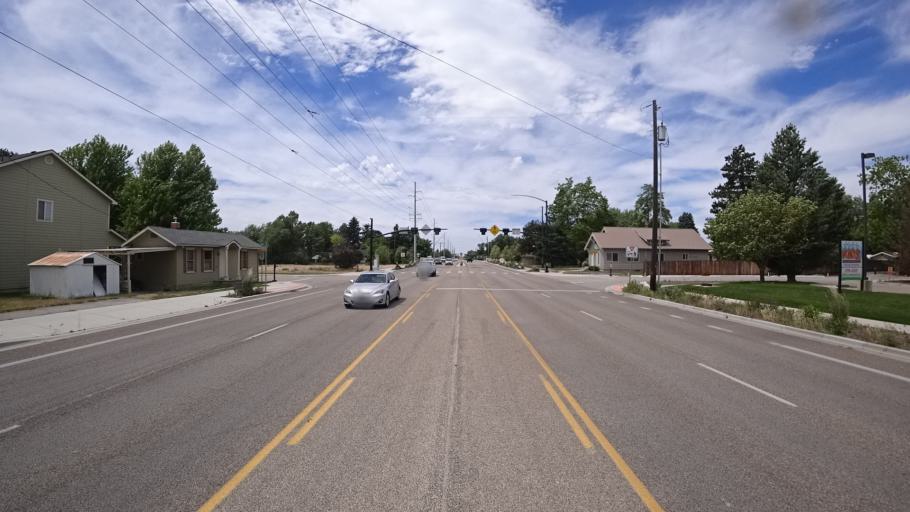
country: US
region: Idaho
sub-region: Ada County
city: Eagle
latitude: 43.6339
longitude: -116.3240
